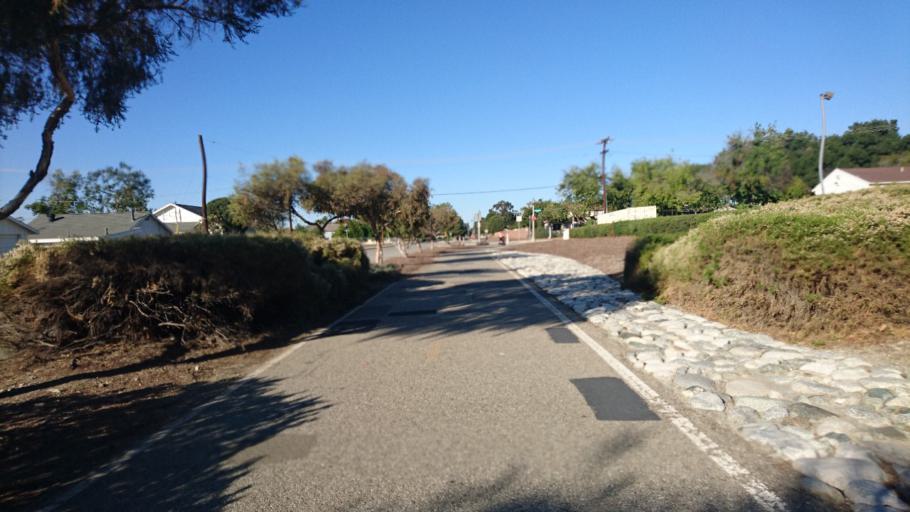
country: US
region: California
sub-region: San Bernardino County
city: Upland
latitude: 34.0979
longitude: -117.6420
